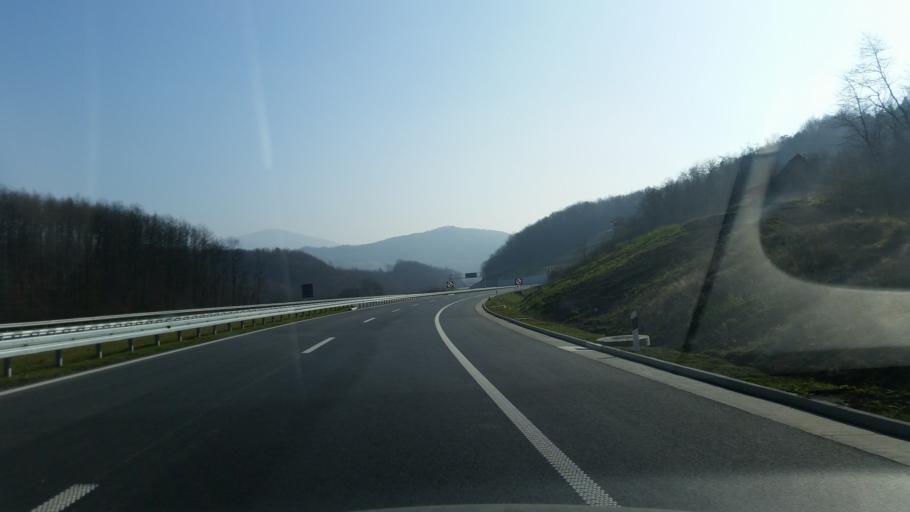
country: RS
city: Prislonica
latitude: 44.0112
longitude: 20.3835
